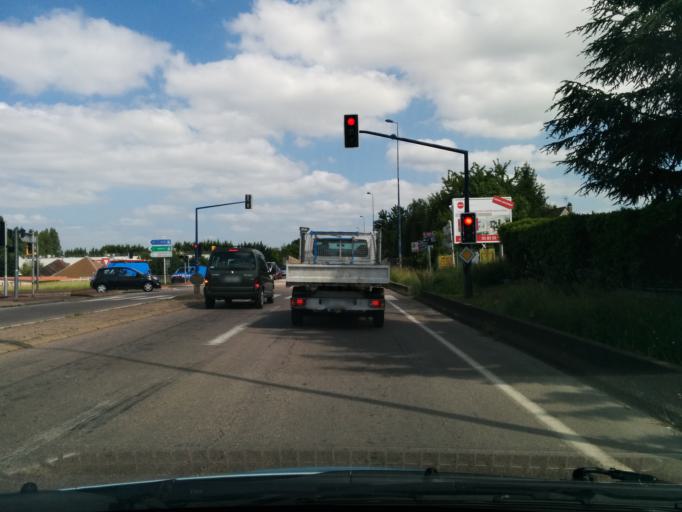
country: FR
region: Ile-de-France
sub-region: Departement des Yvelines
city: Epone
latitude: 48.9603
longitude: 1.8111
